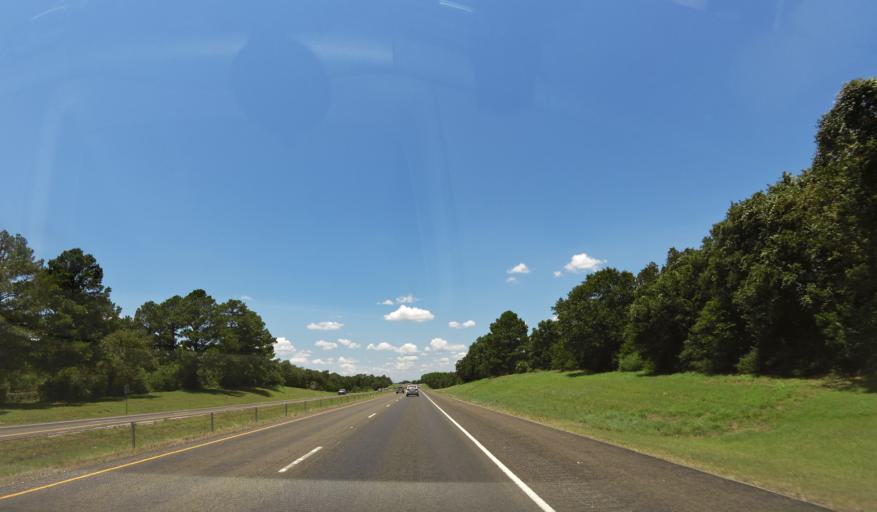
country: US
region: Texas
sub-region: Washington County
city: Brenham
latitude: 30.1814
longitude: -96.4779
